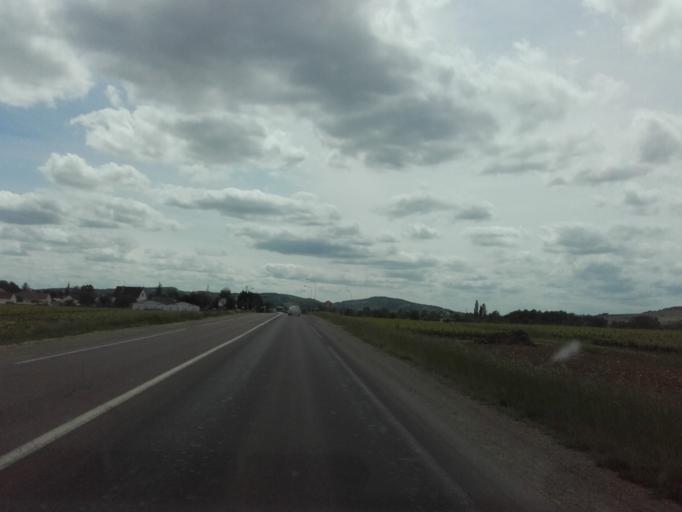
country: FR
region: Bourgogne
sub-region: Departement de la Cote-d'Or
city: Corpeau
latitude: 46.9385
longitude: 4.7567
